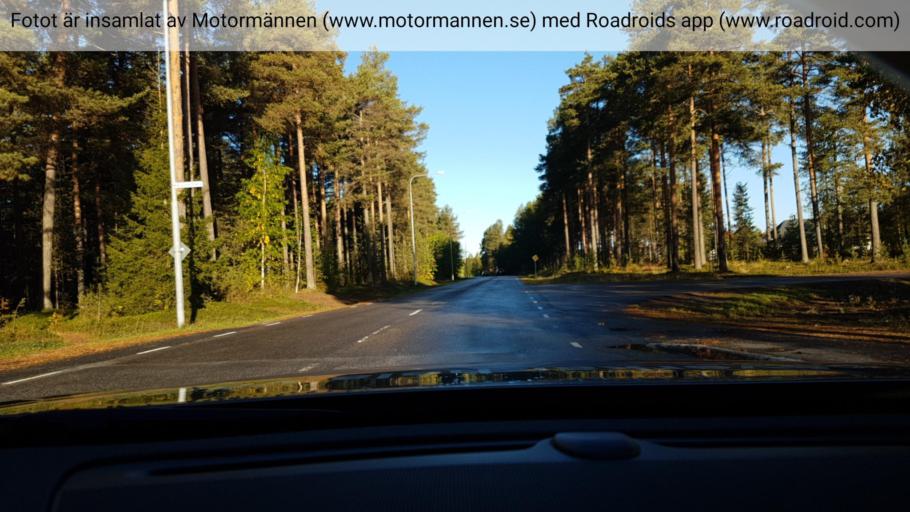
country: SE
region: Norrbotten
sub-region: Lulea Kommun
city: Sodra Sunderbyn
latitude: 65.6508
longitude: 21.9555
